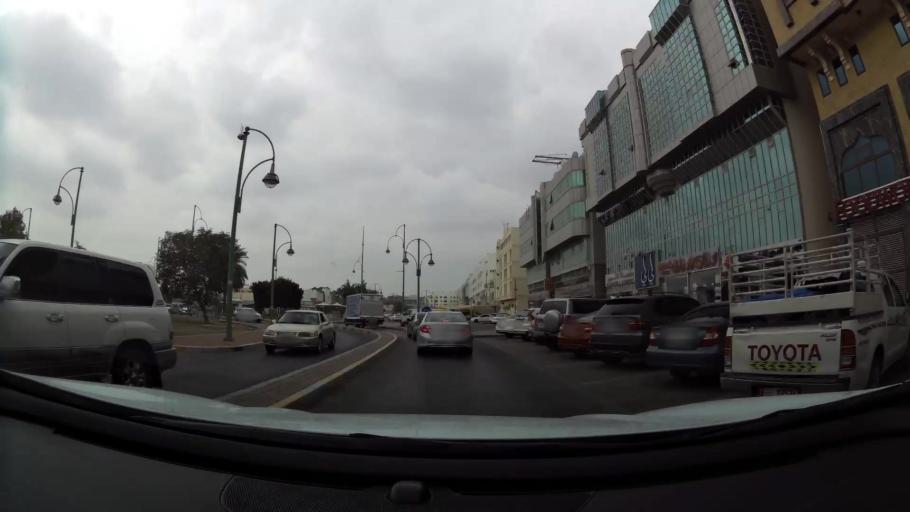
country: AE
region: Abu Dhabi
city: Al Ain
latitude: 24.2213
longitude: 55.7644
